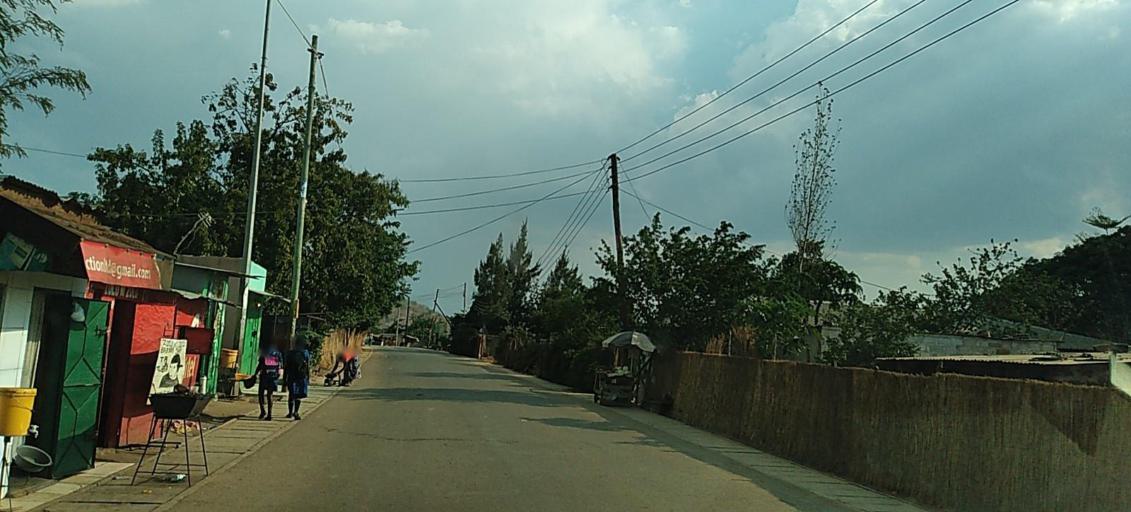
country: ZM
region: Lusaka
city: Lusaka
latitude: -15.5314
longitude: 28.2367
